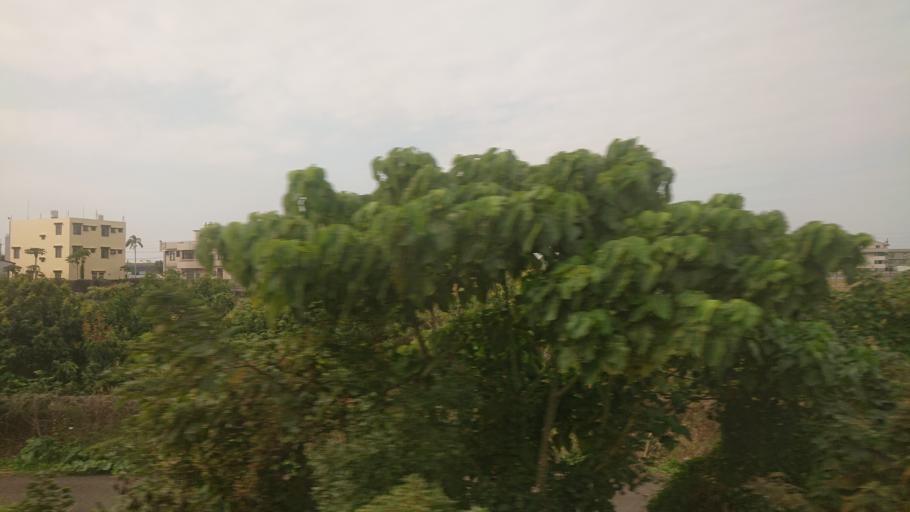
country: TW
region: Taiwan
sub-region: Changhua
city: Chang-hua
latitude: 24.0298
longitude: 120.5350
